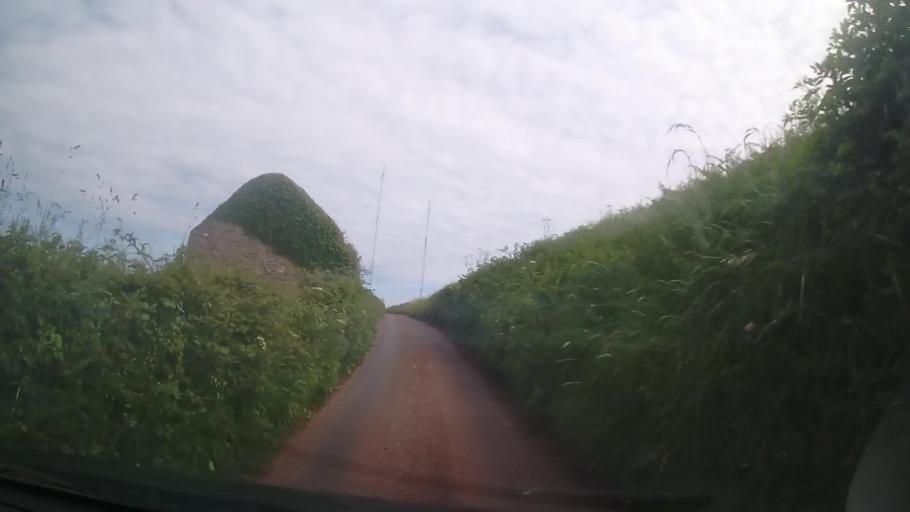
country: GB
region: England
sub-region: Devon
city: Salcombe
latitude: 50.2314
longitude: -3.6691
